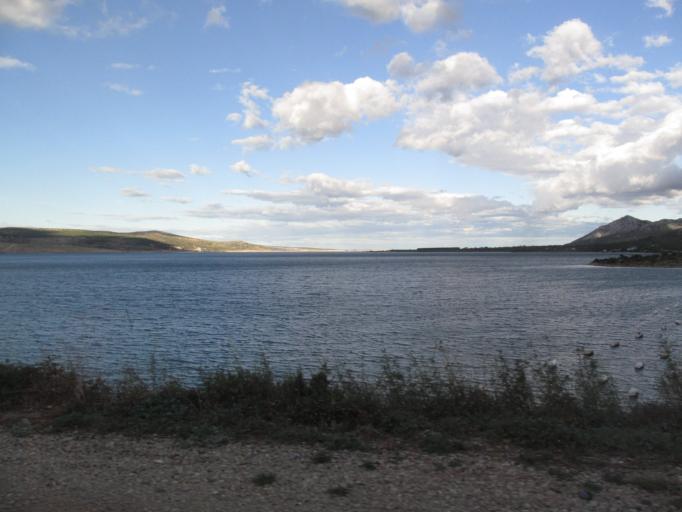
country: HR
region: Zadarska
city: Posedarje
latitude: 44.2621
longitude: 15.5315
